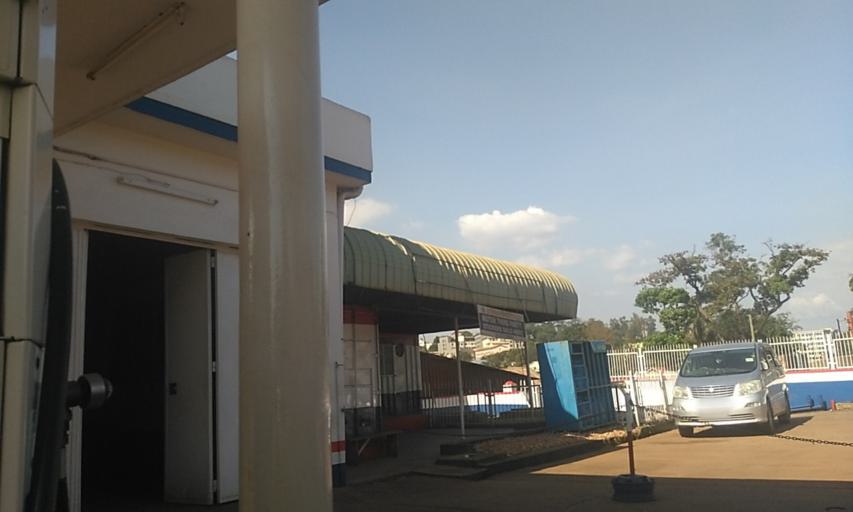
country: UG
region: Central Region
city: Kampala Central Division
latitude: 0.3322
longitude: 32.5754
